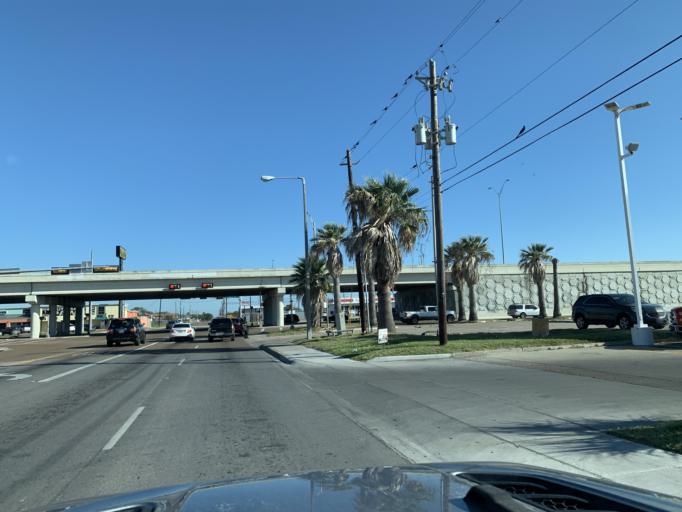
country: US
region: Texas
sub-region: Nueces County
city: Corpus Christi
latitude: 27.6678
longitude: -97.2827
